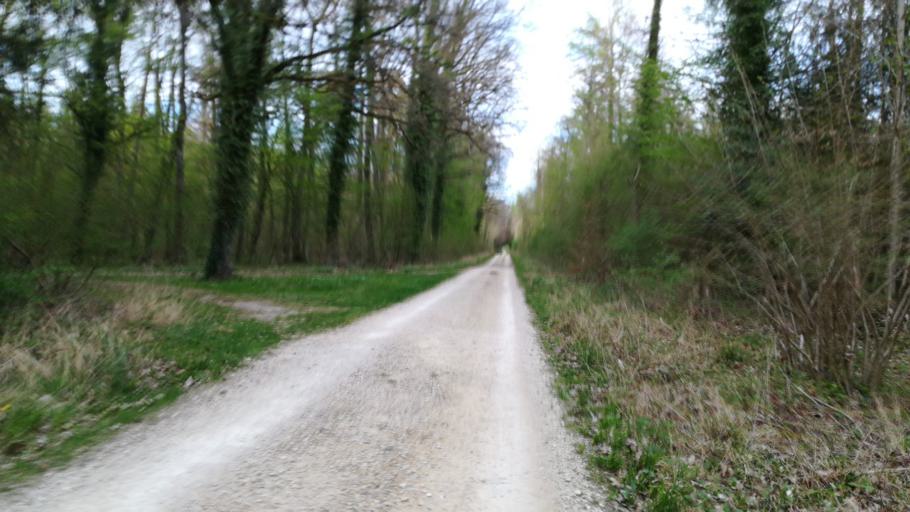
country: DE
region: Baden-Wuerttemberg
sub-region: Freiburg Region
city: Singen
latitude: 47.7485
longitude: 8.8121
